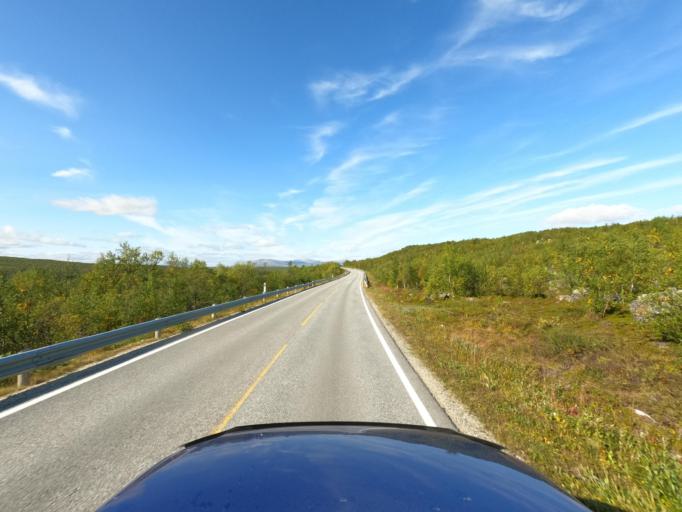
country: NO
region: Finnmark Fylke
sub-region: Porsanger
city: Lakselv
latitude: 69.7656
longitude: 25.1782
